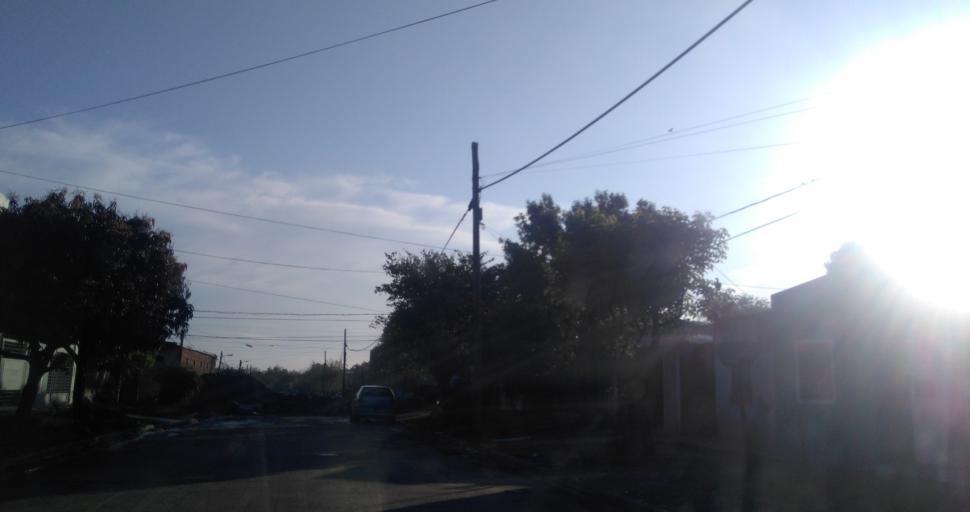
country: AR
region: Chaco
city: Resistencia
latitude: -27.4638
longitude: -58.9697
